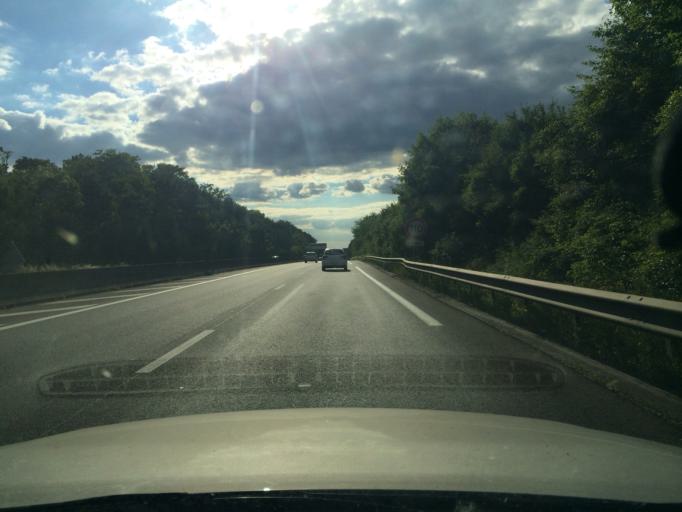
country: FR
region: Lorraine
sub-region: Departement de Meurthe-et-Moselle
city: Ludres
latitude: 48.6440
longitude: 6.1534
